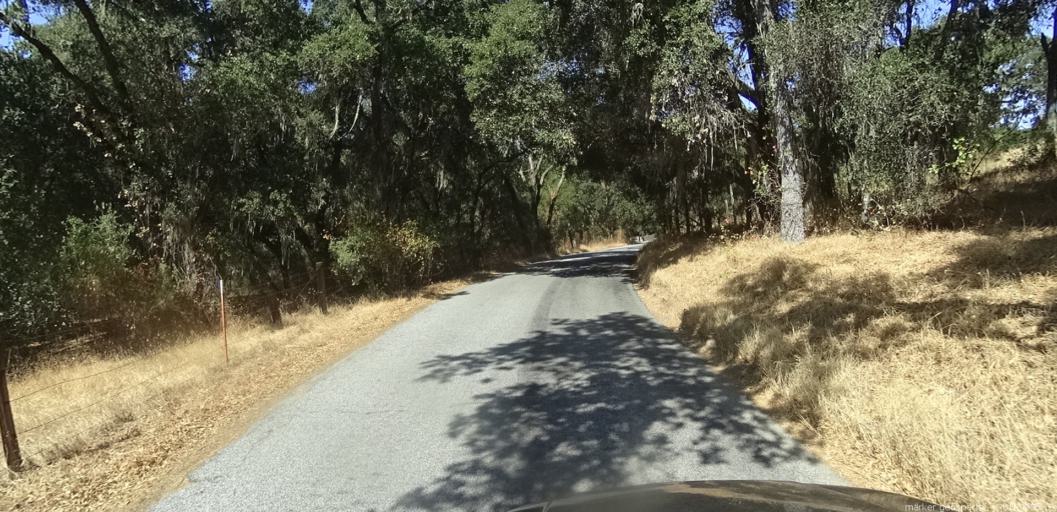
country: US
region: California
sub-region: Monterey County
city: Carmel Valley Village
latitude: 36.4090
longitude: -121.6703
